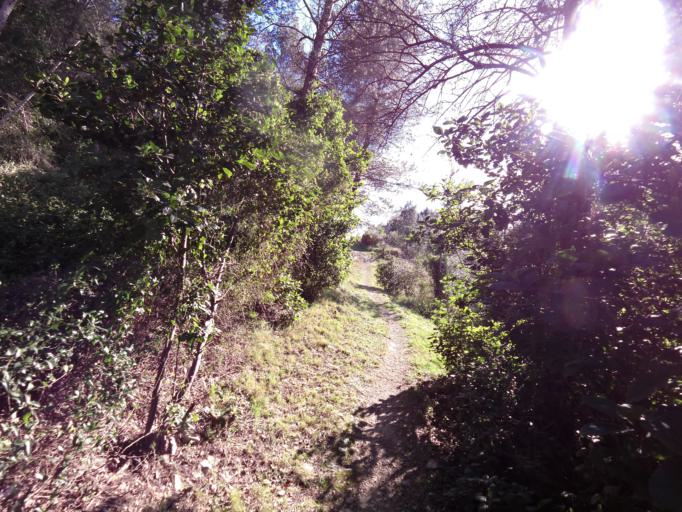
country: FR
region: Languedoc-Roussillon
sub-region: Departement du Gard
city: Calvisson
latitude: 43.7826
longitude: 4.1879
